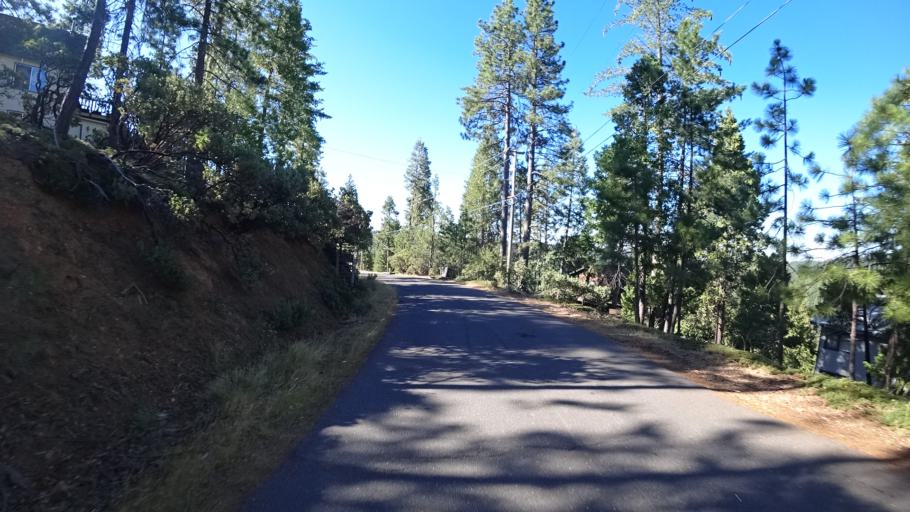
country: US
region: California
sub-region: Calaveras County
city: Arnold
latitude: 38.2639
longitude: -120.3252
